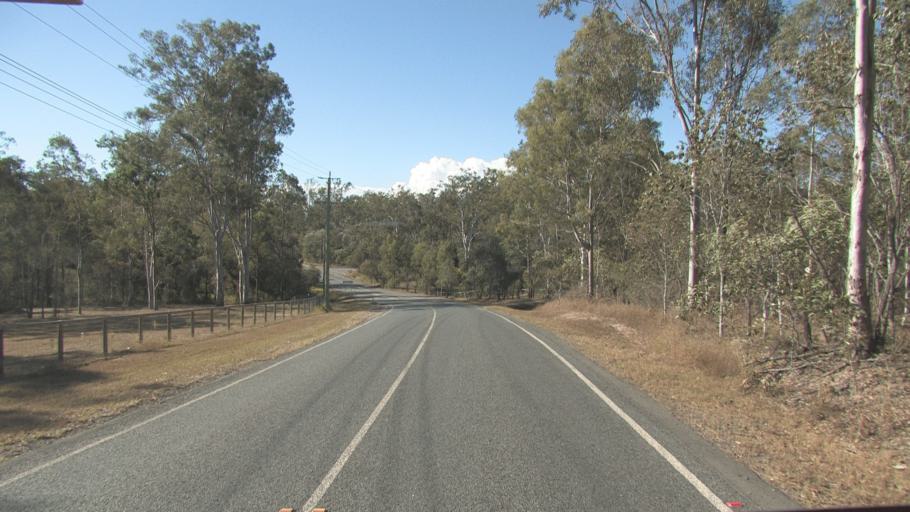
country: AU
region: Queensland
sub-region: Logan
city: Cedar Vale
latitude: -27.8347
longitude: 153.0516
